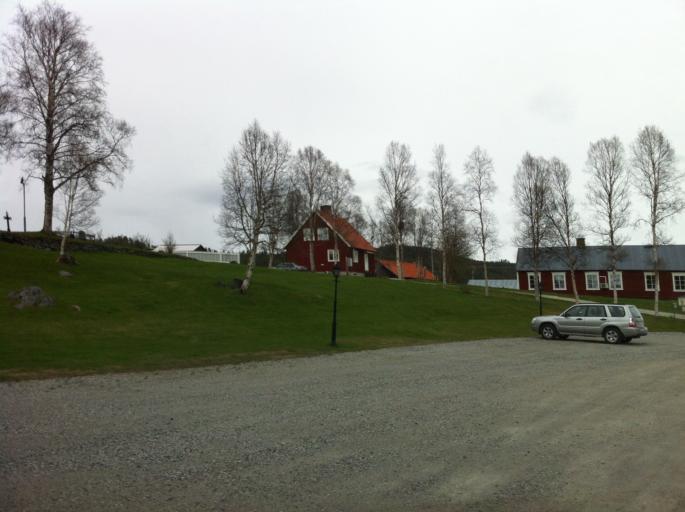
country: SE
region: Jaemtland
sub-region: Are Kommun
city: Are
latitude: 62.5298
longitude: 12.6006
